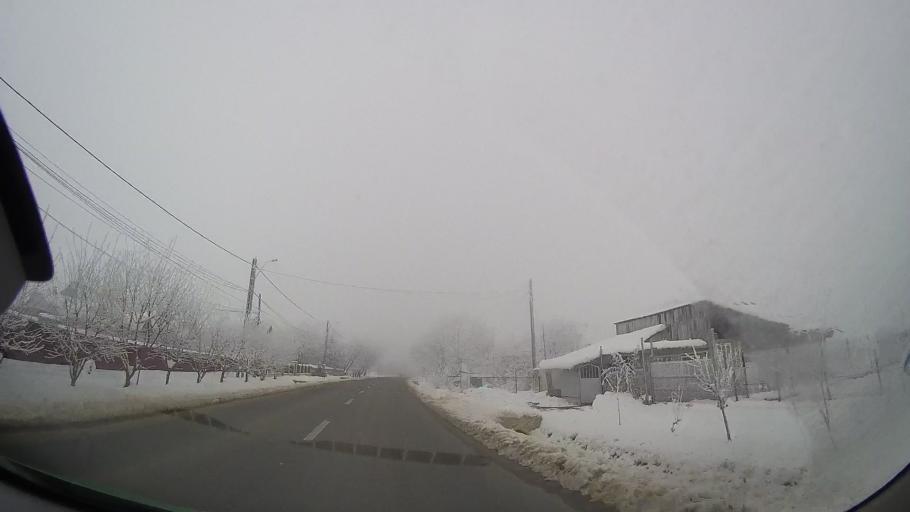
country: RO
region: Iasi
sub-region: Comuna Mogosesti-Siret
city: Mogosesti-Siret
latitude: 47.1623
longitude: 26.7720
